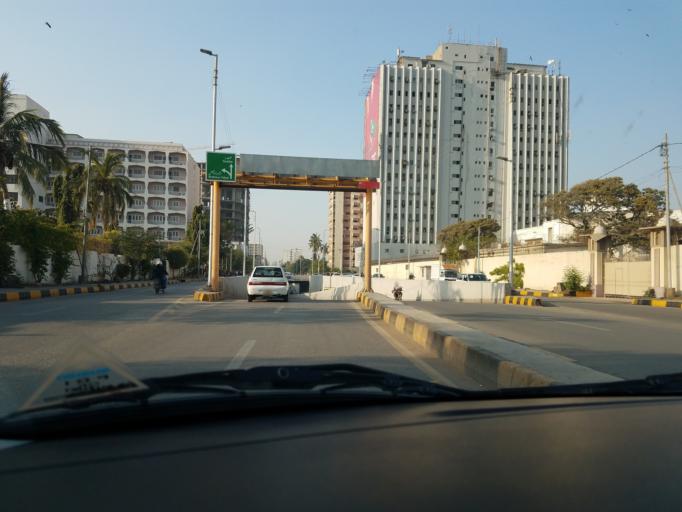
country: PK
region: Sindh
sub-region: Karachi District
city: Karachi
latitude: 24.8510
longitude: 67.0349
